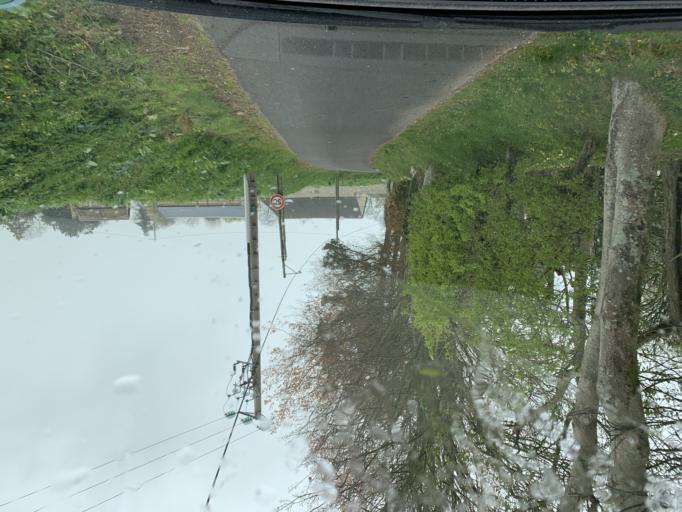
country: FR
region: Haute-Normandie
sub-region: Departement de la Seine-Maritime
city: Etretat
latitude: 49.6845
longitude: 0.1788
